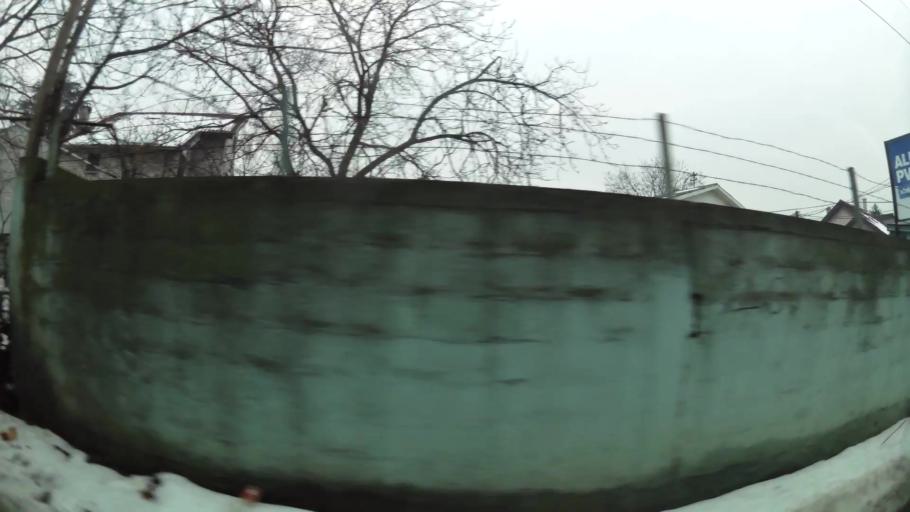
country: RS
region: Central Serbia
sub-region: Belgrade
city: Vozdovac
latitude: 44.7795
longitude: 20.4927
